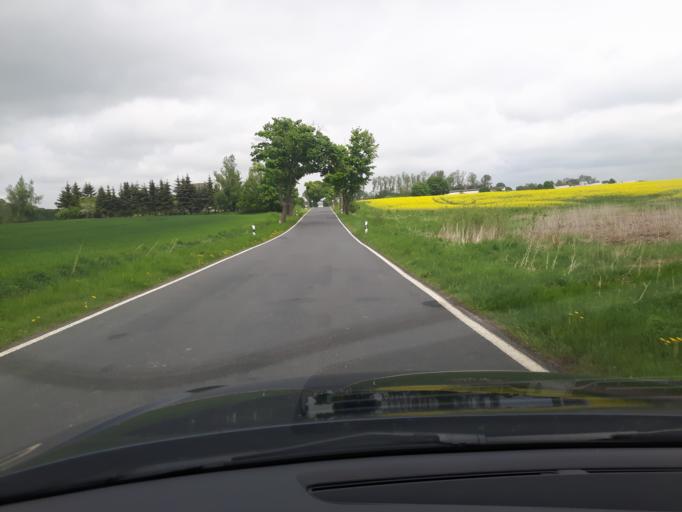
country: DE
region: Mecklenburg-Vorpommern
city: Tribsees
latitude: 54.1855
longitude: 12.7400
